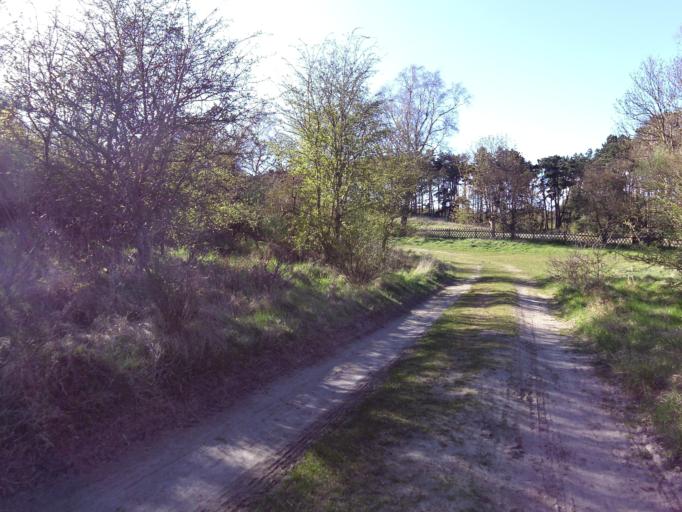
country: DE
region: Mecklenburg-Vorpommern
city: Hiddensee
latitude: 54.6012
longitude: 13.1257
